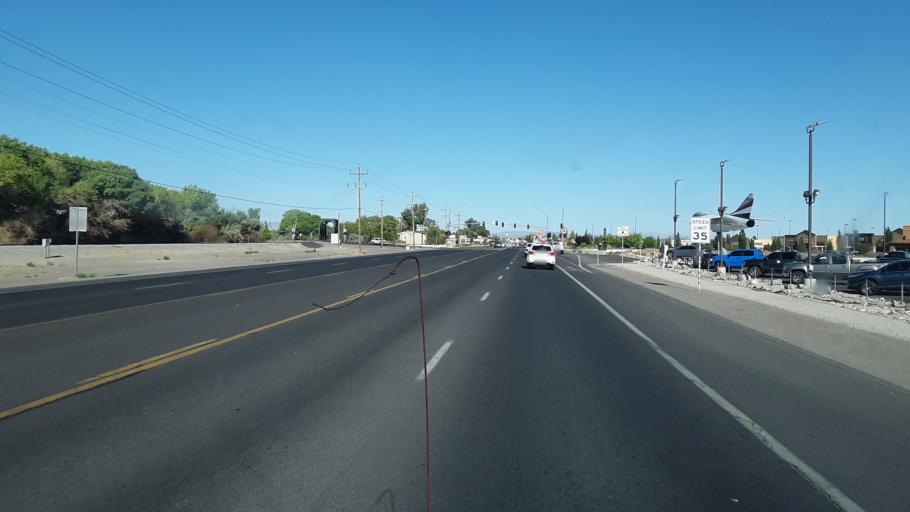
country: US
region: Nevada
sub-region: Churchill County
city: Fallon
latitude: 39.4788
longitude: -118.8107
